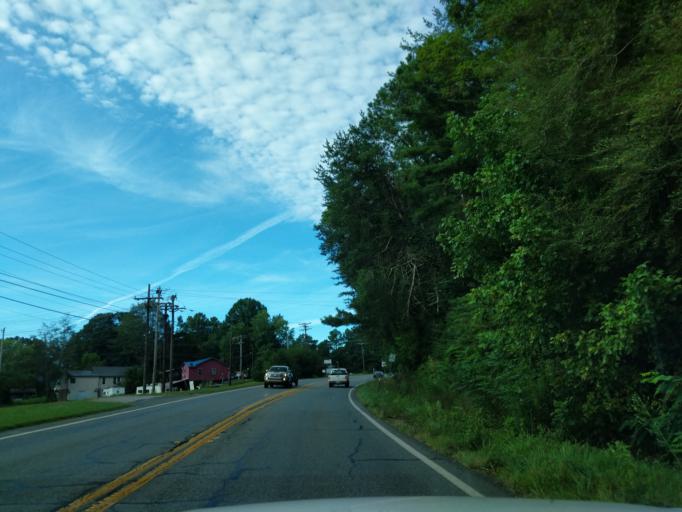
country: US
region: Georgia
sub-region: Fannin County
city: McCaysville
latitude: 34.9490
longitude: -84.3706
